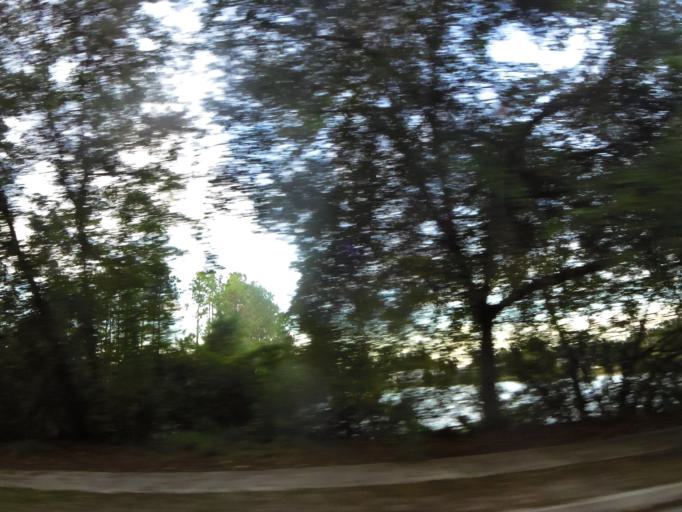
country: US
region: Florida
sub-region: Saint Johns County
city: Fruit Cove
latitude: 30.1552
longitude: -81.5385
